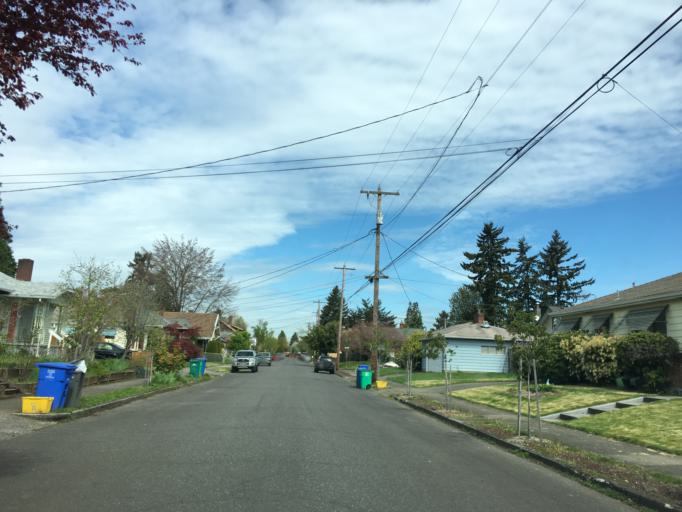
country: US
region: Oregon
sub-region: Multnomah County
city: Lents
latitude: 45.5272
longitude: -122.5914
